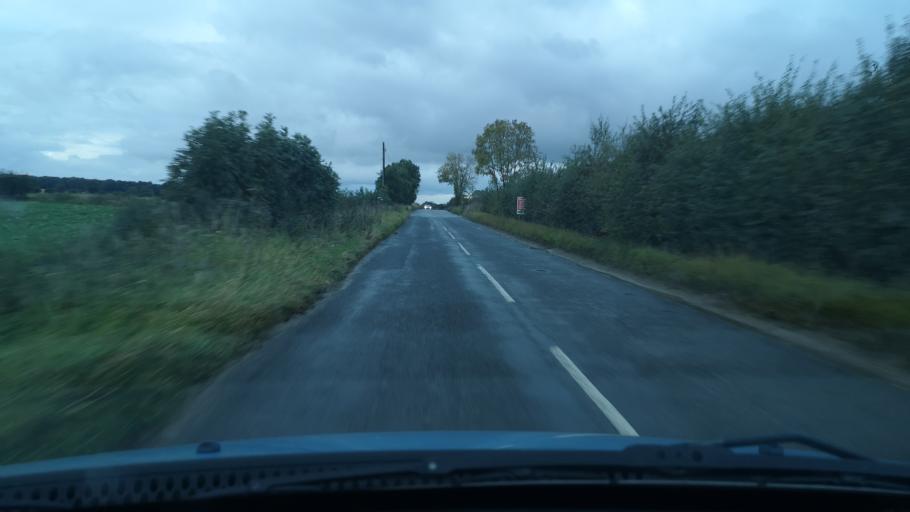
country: GB
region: England
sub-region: City and Borough of Wakefield
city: Darrington
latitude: 53.6463
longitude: -1.2475
